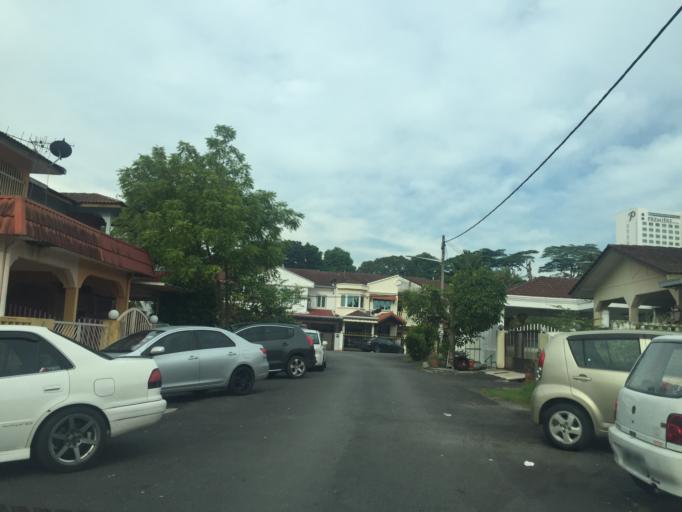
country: MY
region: Selangor
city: Klang
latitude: 3.0048
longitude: 101.4436
